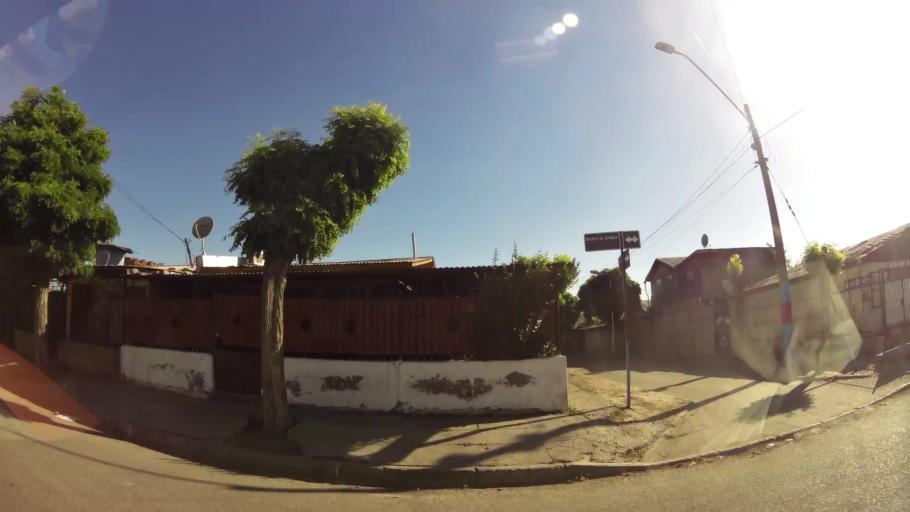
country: CL
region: Santiago Metropolitan
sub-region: Provincia de Maipo
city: San Bernardo
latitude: -33.5913
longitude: -70.6808
